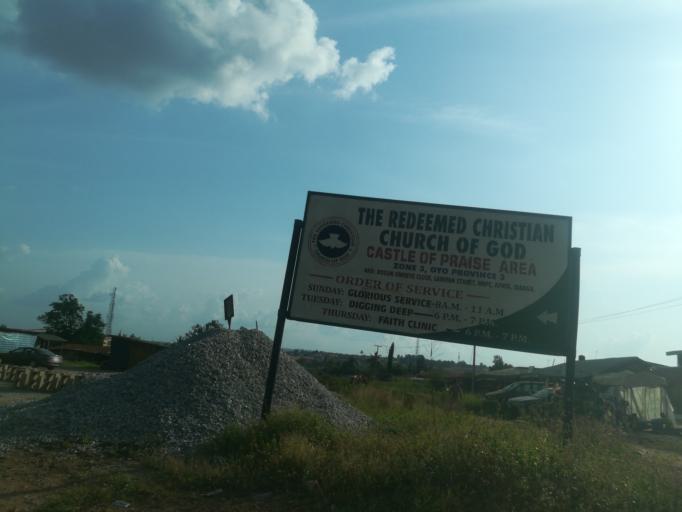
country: NG
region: Oyo
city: Ibadan
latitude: 7.3868
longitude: 3.8186
